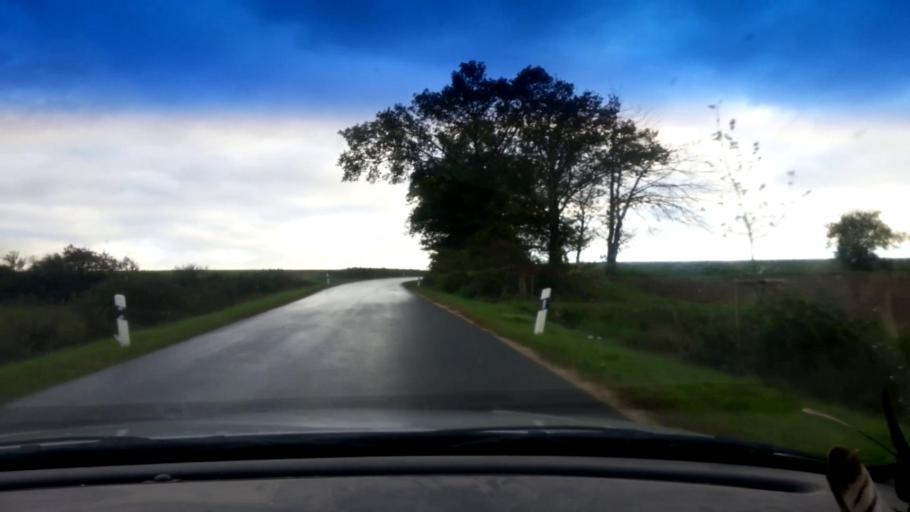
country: DE
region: Bavaria
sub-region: Upper Franconia
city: Burgwindheim
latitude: 49.8145
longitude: 10.6539
